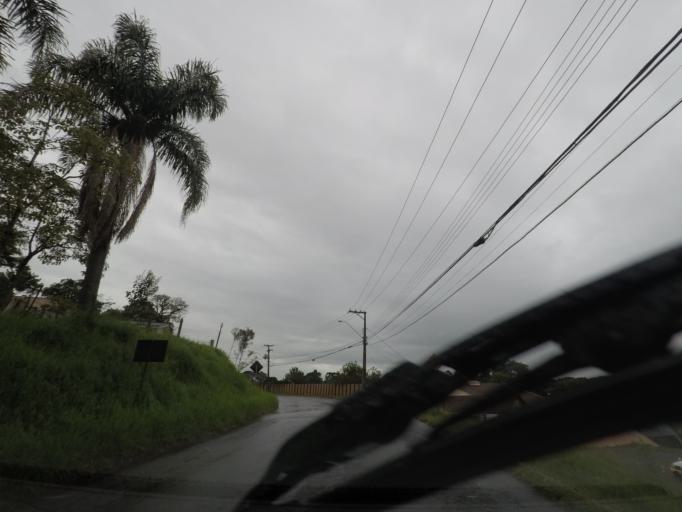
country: BR
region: Parana
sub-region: Curitiba
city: Curitiba
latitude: -25.4628
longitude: -49.3935
